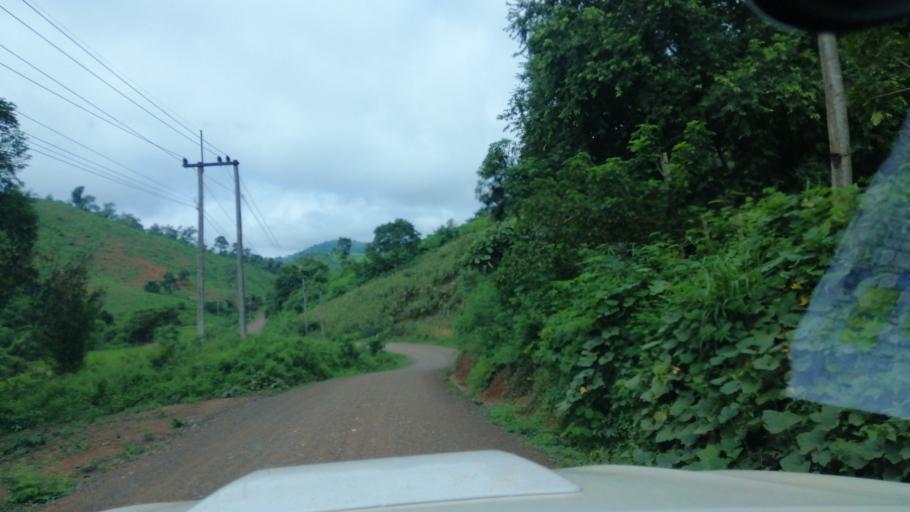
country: LA
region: Xiagnabouli
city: Muang Kenthao
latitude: 17.9175
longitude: 101.3692
